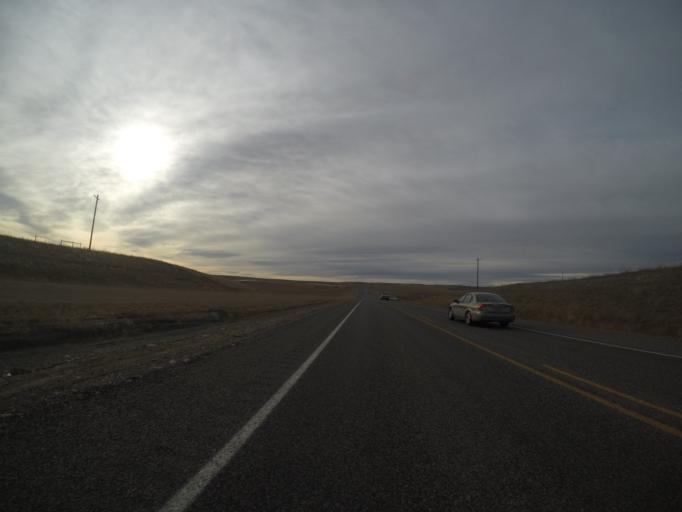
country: US
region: Montana
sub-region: Yellowstone County
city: Laurel
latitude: 45.5651
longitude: -108.8534
